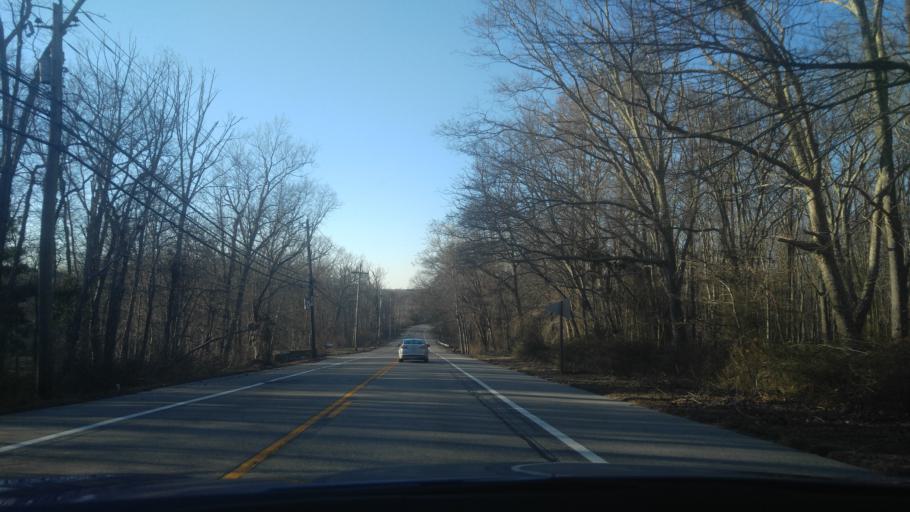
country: US
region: Rhode Island
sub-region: Washington County
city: North Kingstown
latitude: 41.5341
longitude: -71.4331
